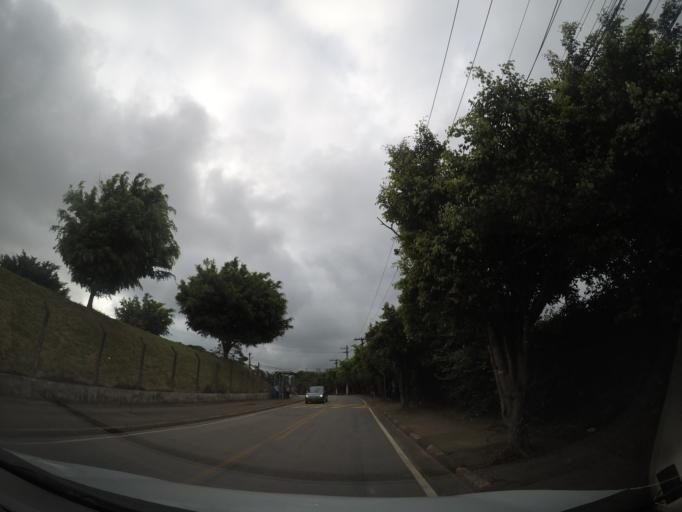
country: BR
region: Sao Paulo
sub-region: Aruja
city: Aruja
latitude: -23.4031
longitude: -46.3537
